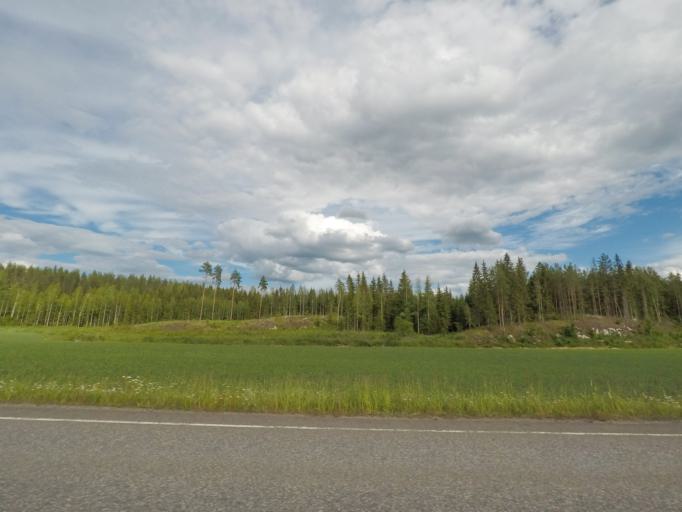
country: FI
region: Paijanne Tavastia
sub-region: Lahti
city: Hollola
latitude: 60.8384
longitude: 25.4934
